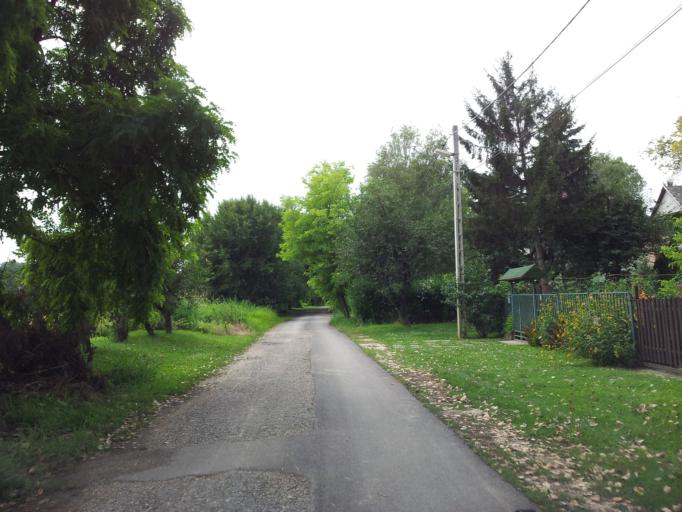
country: HU
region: Pest
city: Szigetujfalu
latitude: 47.2177
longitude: 18.9685
